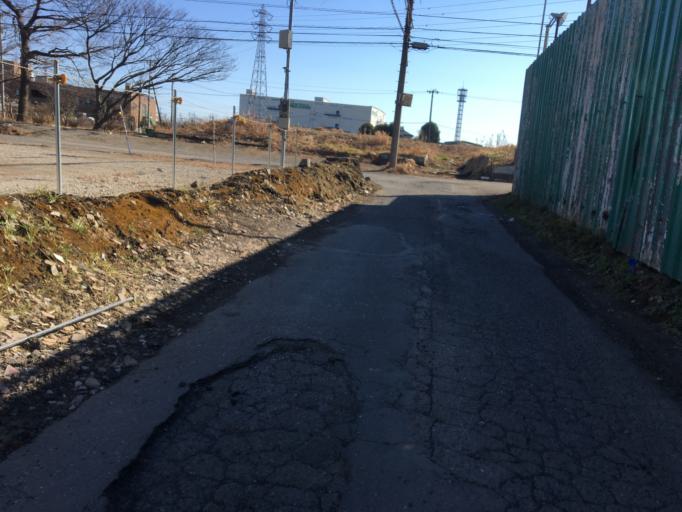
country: JP
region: Saitama
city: Oi
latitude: 35.8130
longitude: 139.5335
